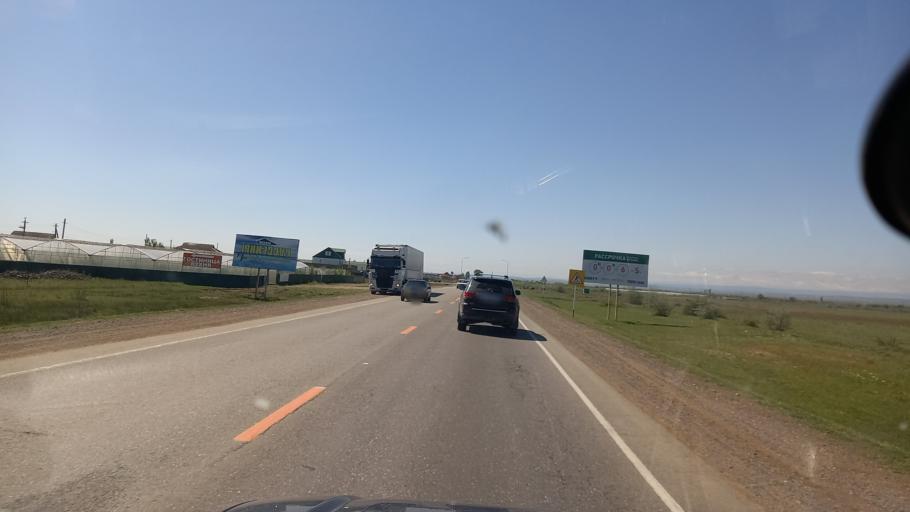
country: RU
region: Dagestan
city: Khazar
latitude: 41.9353
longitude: 48.3269
